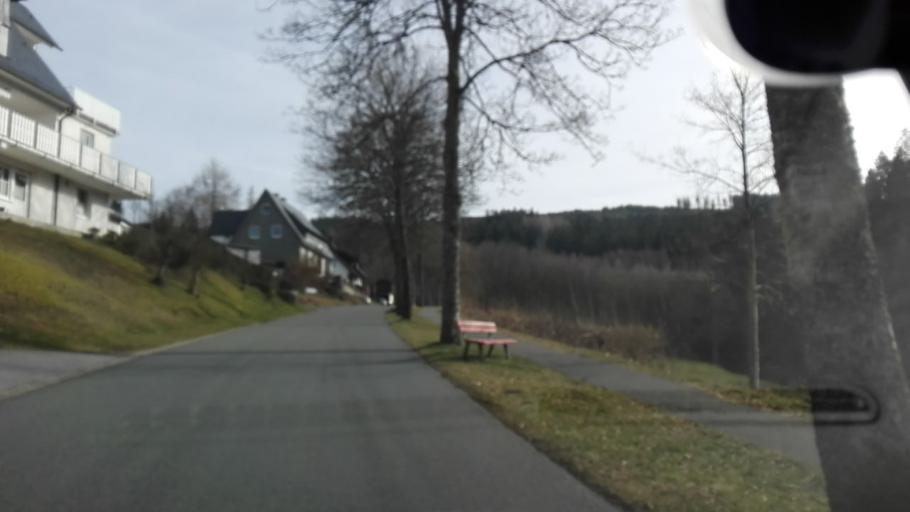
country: DE
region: North Rhine-Westphalia
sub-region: Regierungsbezirk Arnsberg
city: Schmallenberg
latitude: 51.1413
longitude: 8.3326
